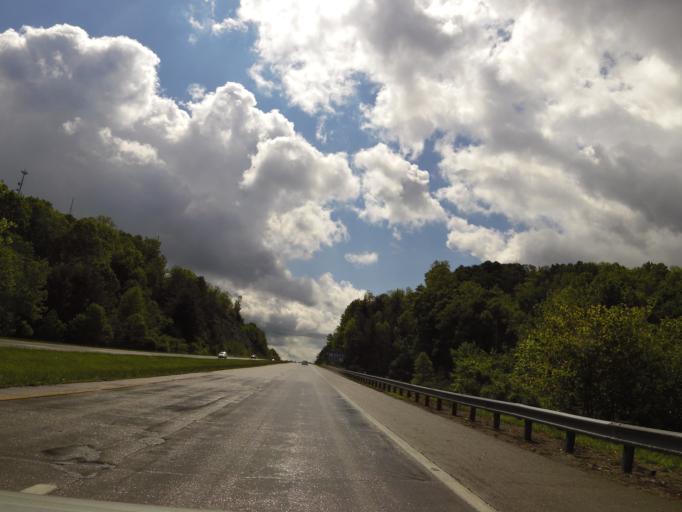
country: US
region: Ohio
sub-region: Athens County
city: Athens
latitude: 39.3553
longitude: -82.0959
